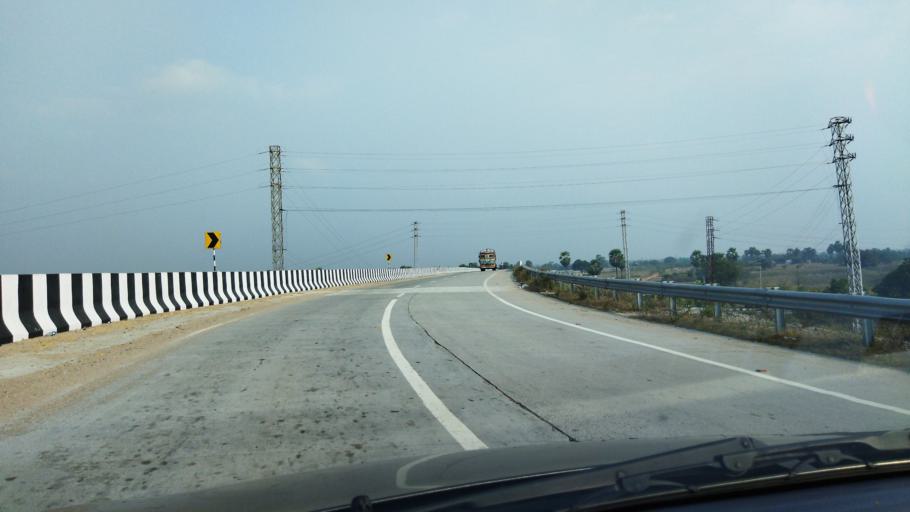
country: IN
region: Telangana
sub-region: Nalgonda
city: Nalgonda
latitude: 17.1676
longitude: 79.3948
